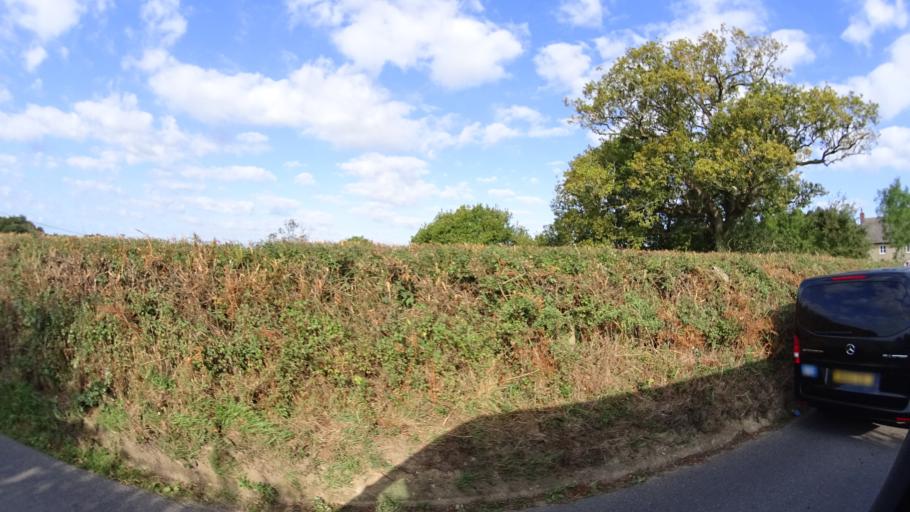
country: GB
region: England
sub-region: Dorset
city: Lytchett Matravers
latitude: 50.7464
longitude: -2.0466
